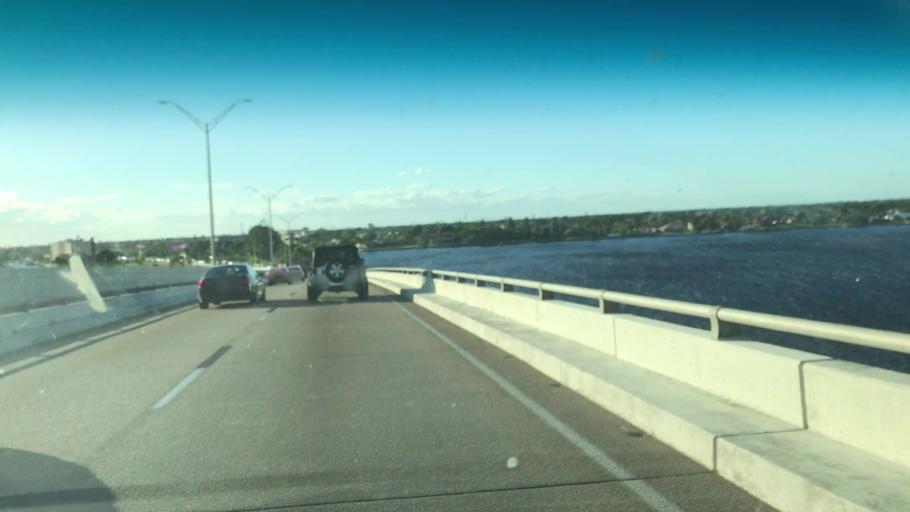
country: US
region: Florida
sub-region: Lee County
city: McGregor
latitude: 26.5615
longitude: -81.9298
